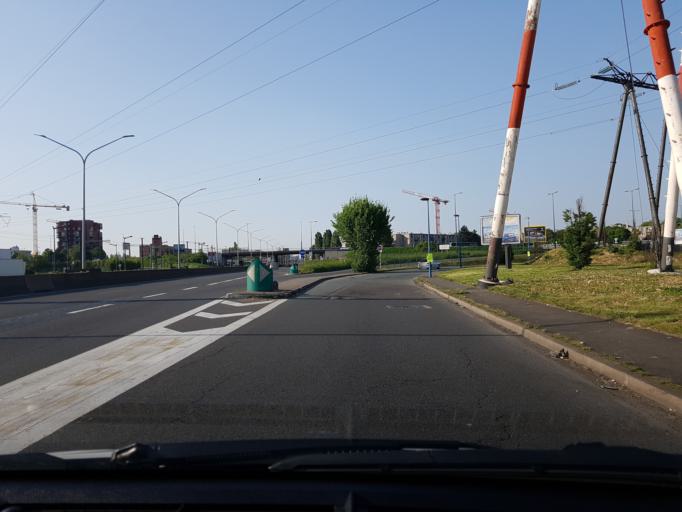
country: FR
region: Ile-de-France
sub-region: Departement du Val-de-Marne
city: Rungis
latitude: 48.7573
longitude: 2.3688
